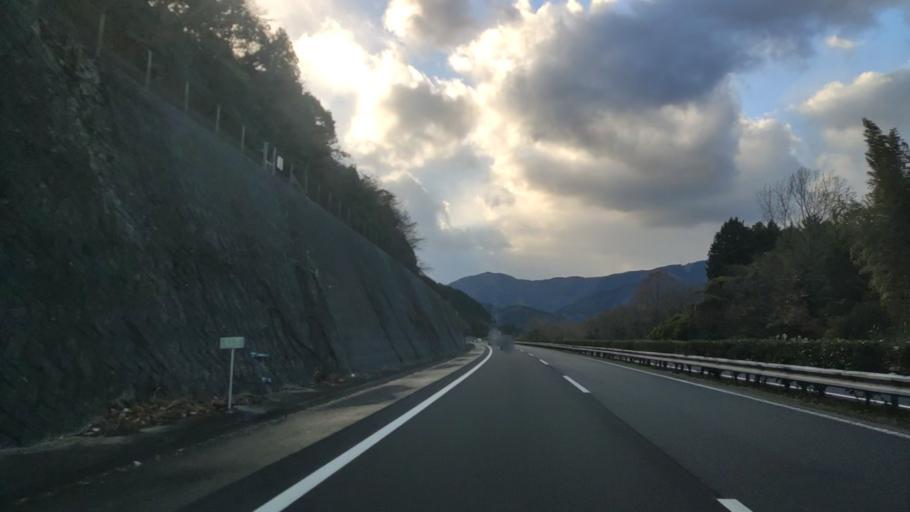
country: JP
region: Ehime
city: Saijo
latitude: 33.8549
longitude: 133.0216
